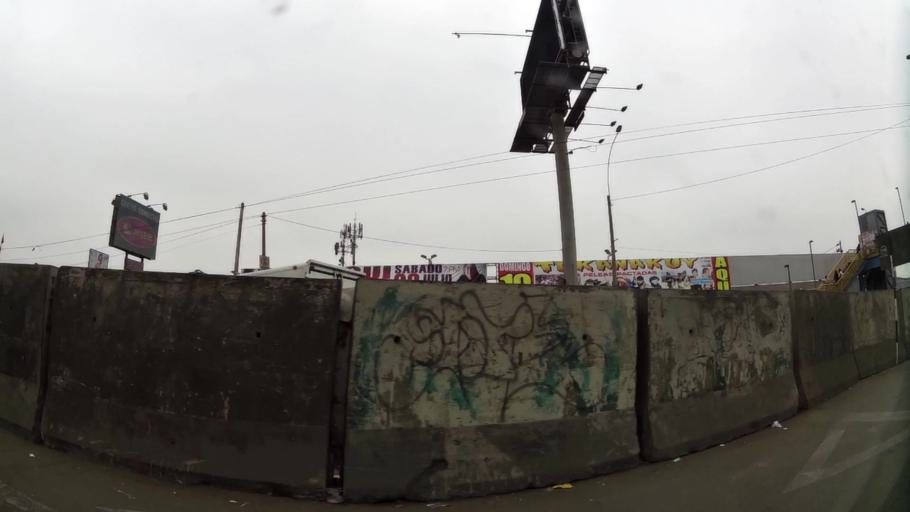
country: PE
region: Lima
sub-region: Lima
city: San Luis
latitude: -12.0585
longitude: -76.9706
